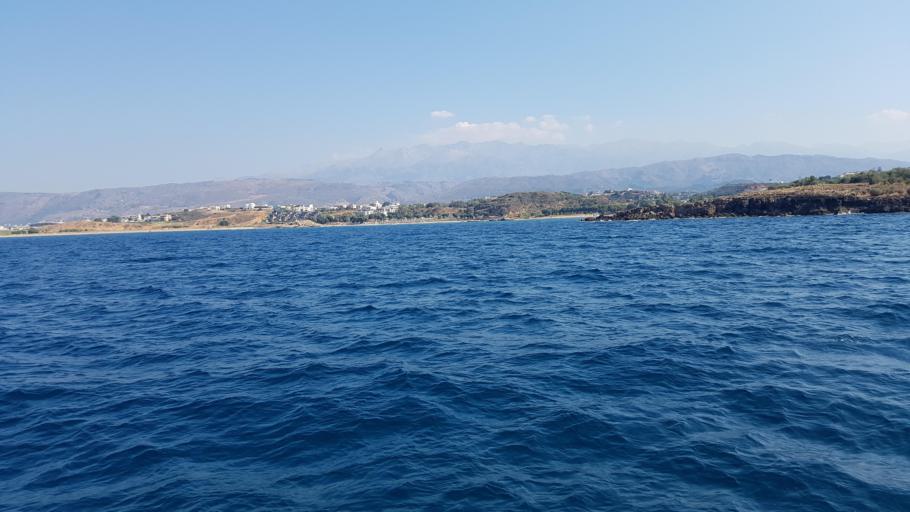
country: GR
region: Crete
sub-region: Nomos Chanias
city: Daratsos
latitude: 35.5193
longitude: 23.9909
